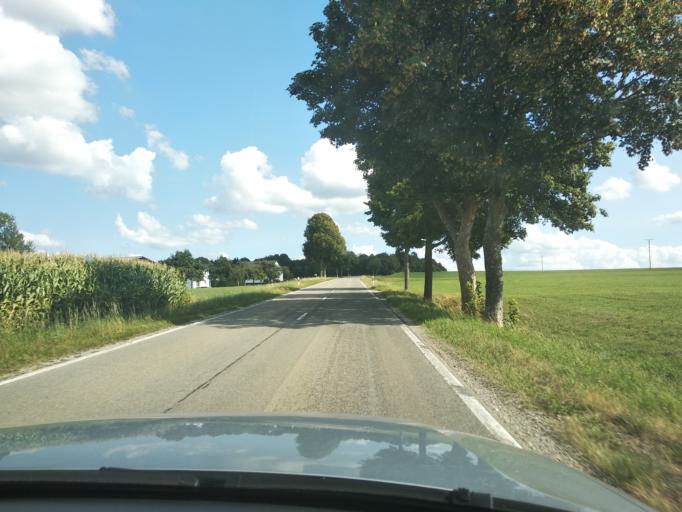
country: DE
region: Baden-Wuerttemberg
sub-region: Tuebingen Region
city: Leutkirch im Allgau
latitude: 47.8849
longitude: 9.9816
